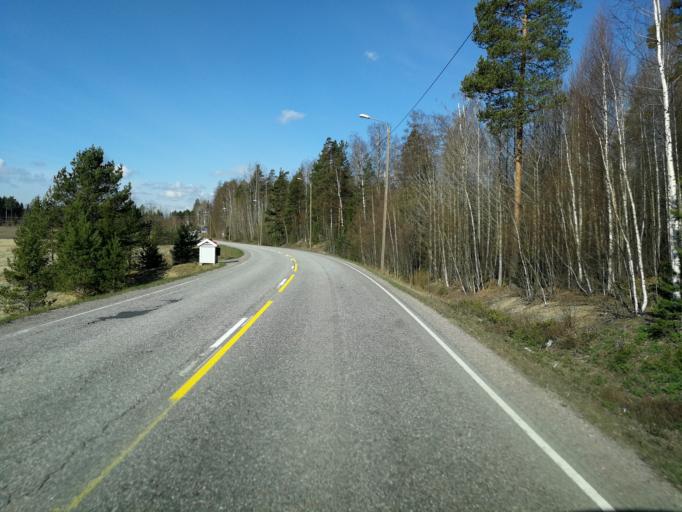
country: FI
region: Uusimaa
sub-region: Helsinki
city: Kirkkonummi
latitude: 60.2047
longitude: 24.4143
